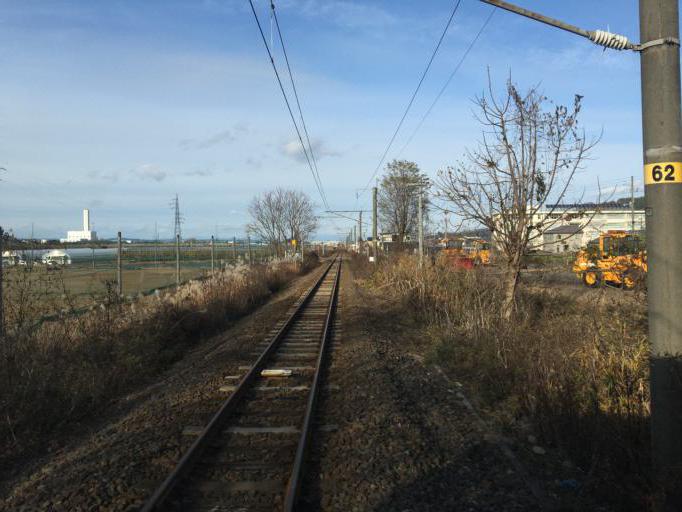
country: JP
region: Akita
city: Yuzawa
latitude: 39.1409
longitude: 140.4857
